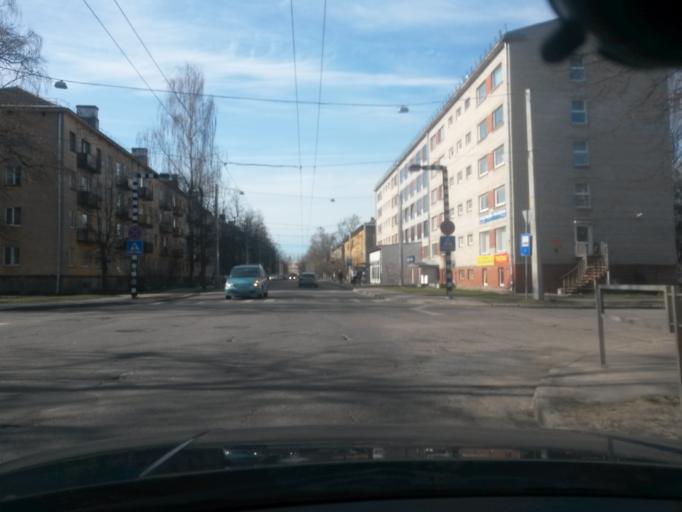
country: LV
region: Kekava
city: Balozi
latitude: 56.9095
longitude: 24.1954
